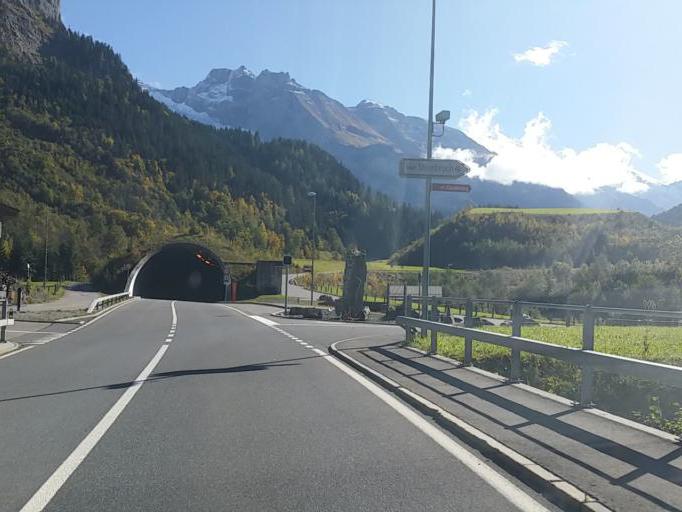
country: CH
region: Bern
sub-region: Frutigen-Niedersimmental District
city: Kandersteg
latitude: 46.5231
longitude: 7.6771
